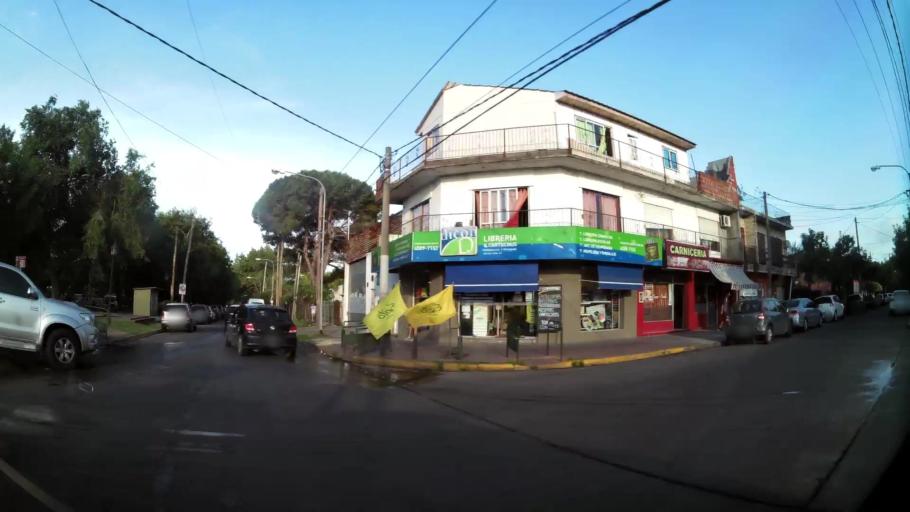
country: AR
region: Buenos Aires
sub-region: Partido de Tigre
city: Tigre
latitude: -34.4558
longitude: -58.6345
